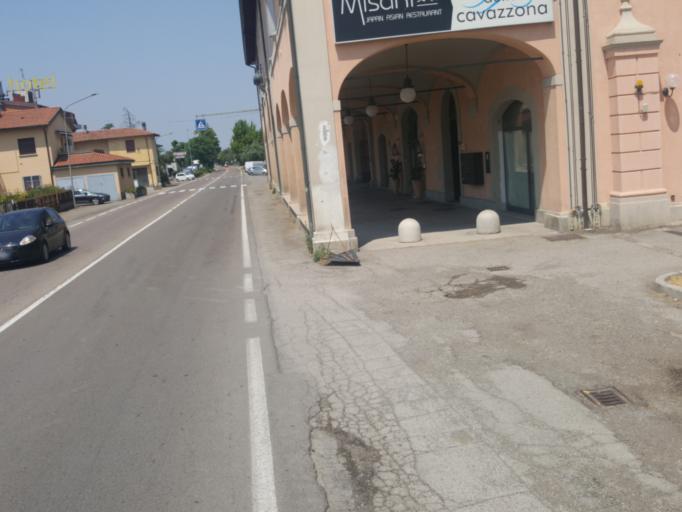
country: IT
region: Emilia-Romagna
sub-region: Provincia di Modena
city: Cavazzona
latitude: 44.5730
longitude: 11.1160
